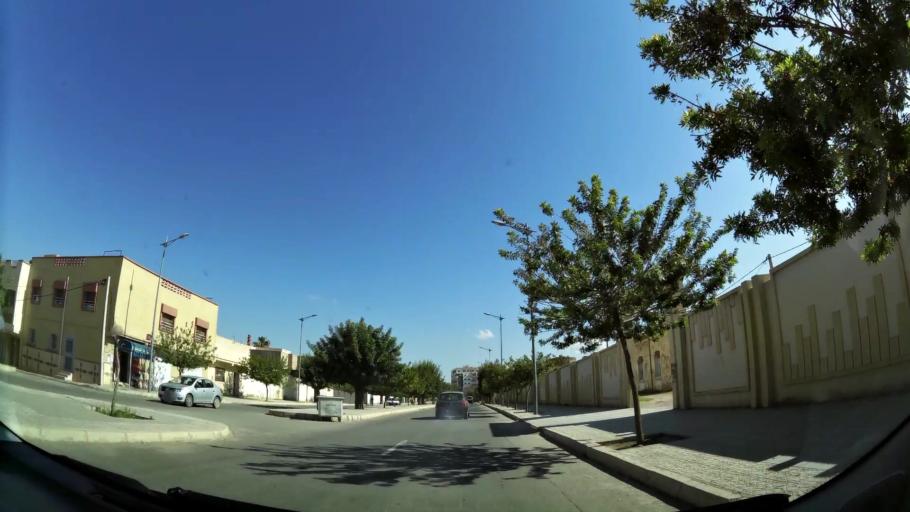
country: MA
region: Oriental
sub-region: Oujda-Angad
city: Oujda
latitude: 34.6916
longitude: -1.9213
